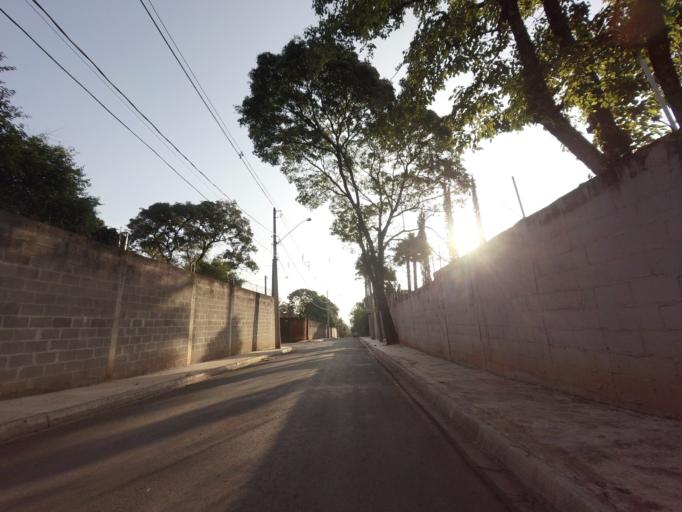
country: BR
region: Sao Paulo
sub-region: Piracicaba
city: Piracicaba
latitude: -22.7468
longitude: -47.6055
